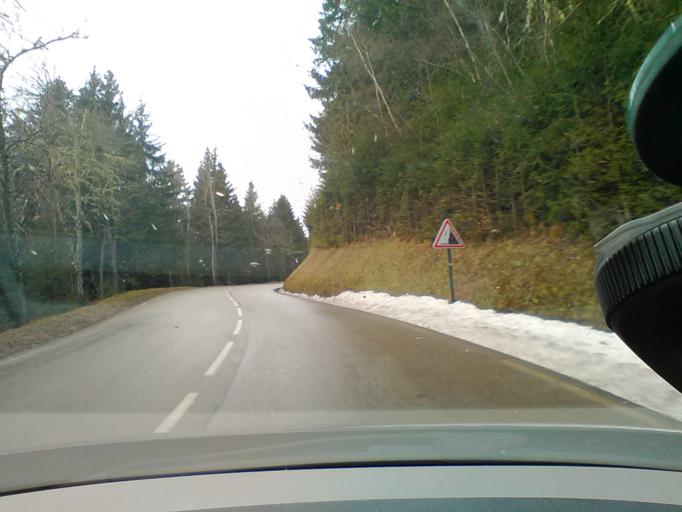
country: FR
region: Rhone-Alpes
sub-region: Departement de l'Isere
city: Theys
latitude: 45.2688
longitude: 6.0051
